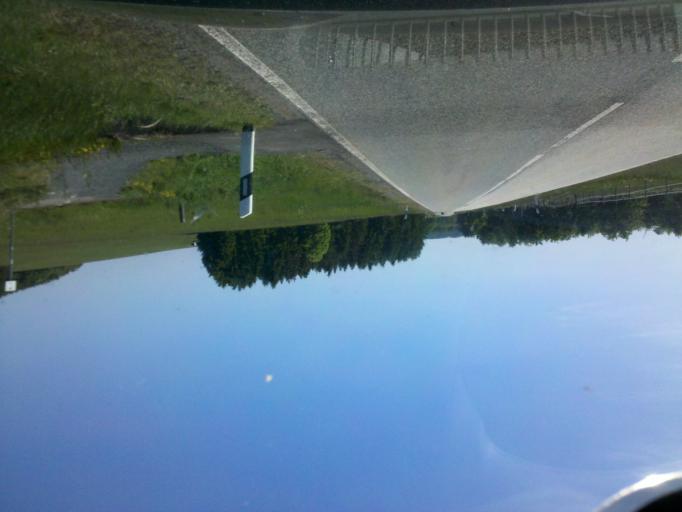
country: DE
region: Rheinland-Pfalz
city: Homberg
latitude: 50.6549
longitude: 8.1039
